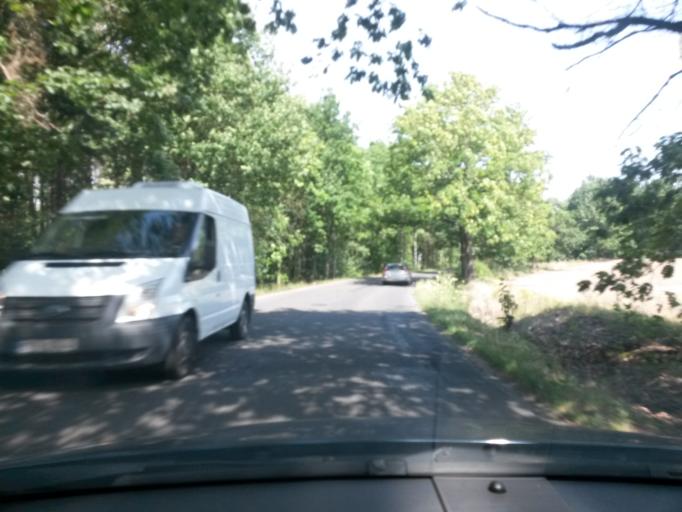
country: PL
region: Lower Silesian Voivodeship
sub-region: Powiat legnicki
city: Prochowice
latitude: 51.2338
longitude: 16.3596
